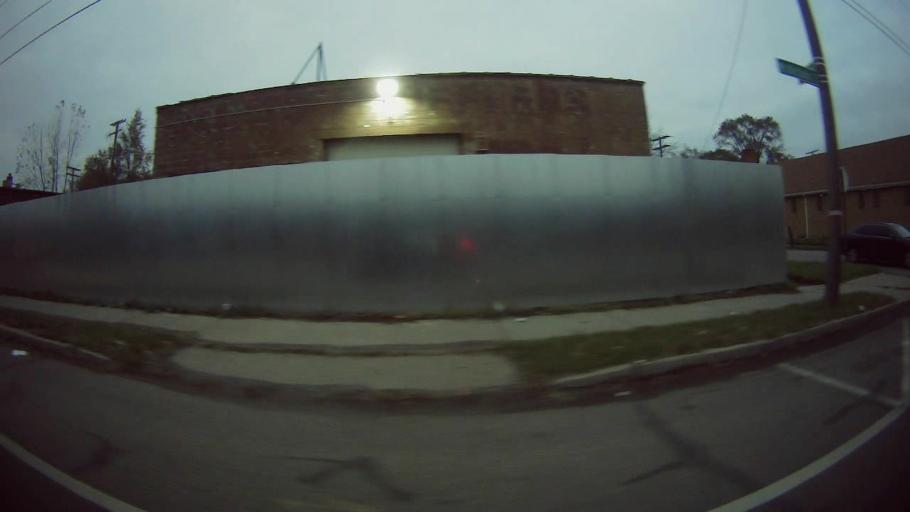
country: US
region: Michigan
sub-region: Wayne County
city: Highland Park
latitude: 42.4186
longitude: -83.0774
